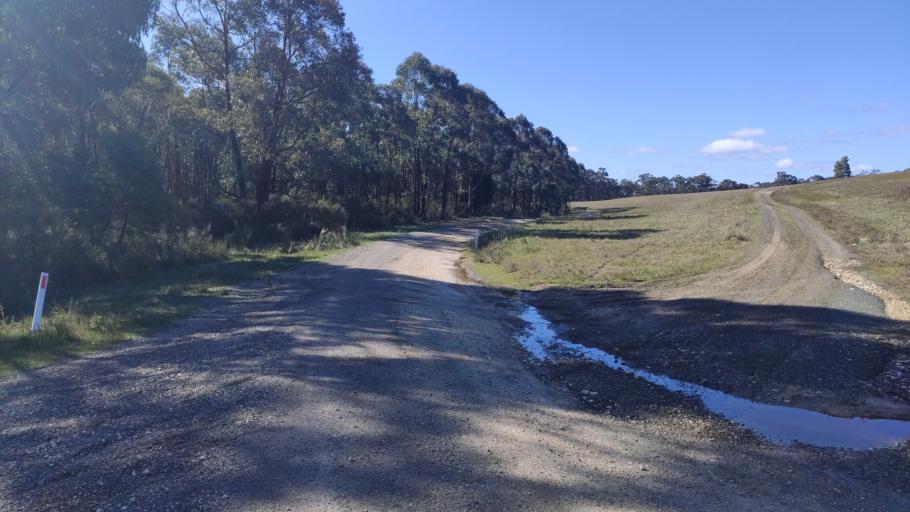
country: AU
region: Victoria
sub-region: Ballarat North
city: Delacombe
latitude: -37.7388
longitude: 143.7525
